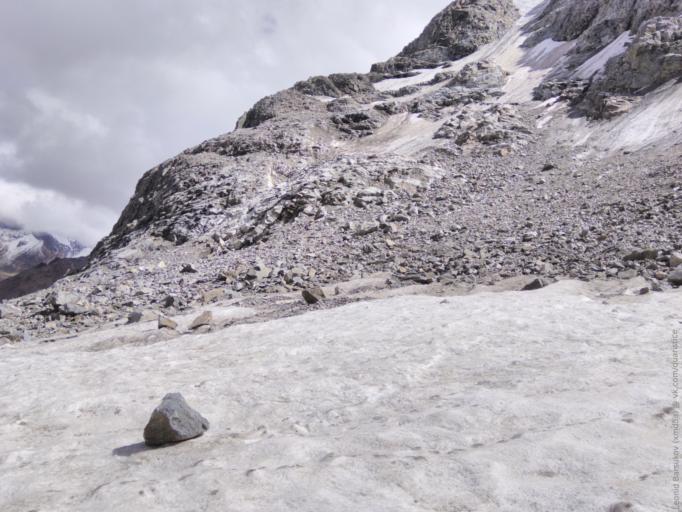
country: RU
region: Karachayevo-Cherkesiya
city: Uchkulan
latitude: 43.3468
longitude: 42.3007
